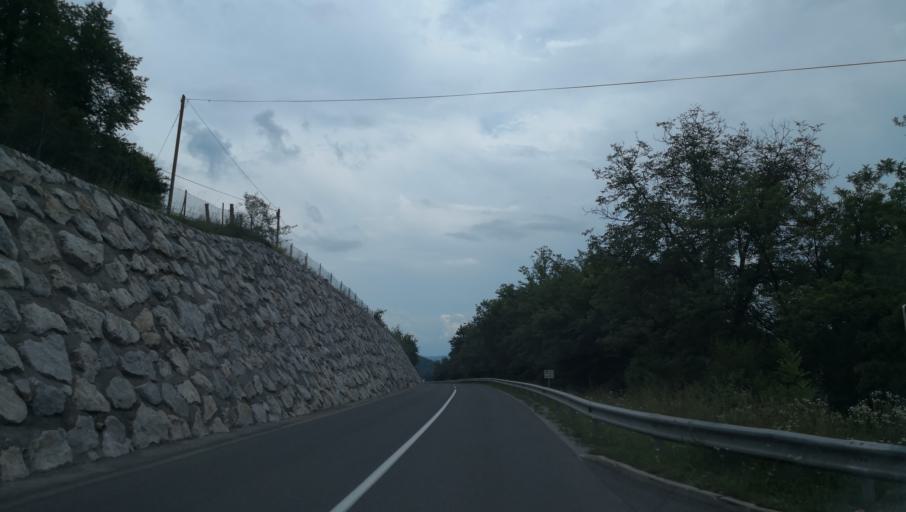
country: SI
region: Zuzemberk
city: Zuzemberk
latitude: 45.8557
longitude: 14.8829
